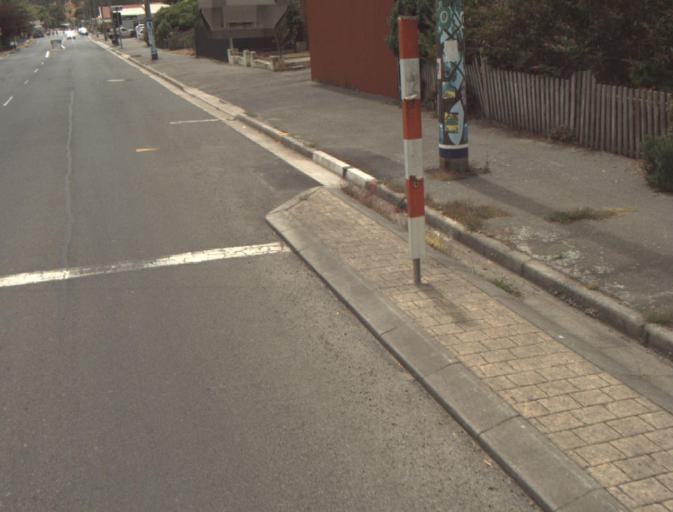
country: AU
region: Tasmania
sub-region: Launceston
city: Mayfield
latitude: -41.2526
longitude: 147.2161
